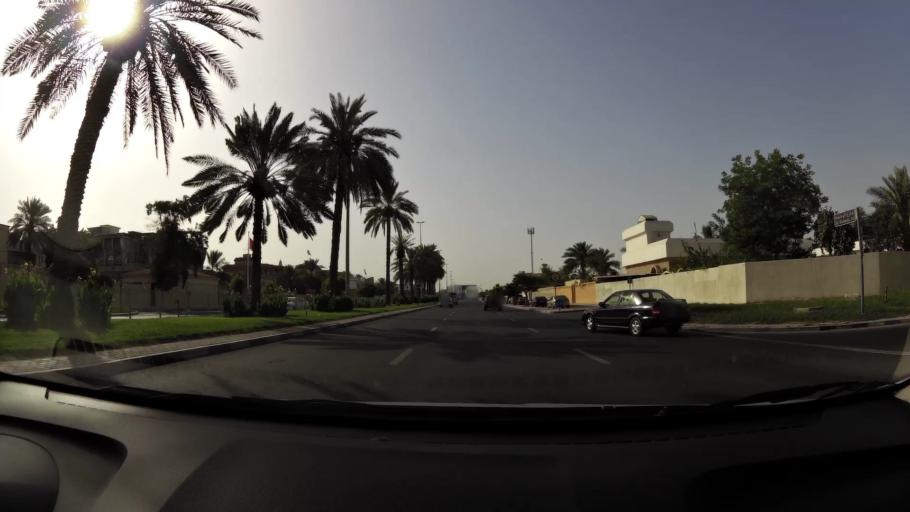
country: AE
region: Ash Shariqah
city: Sharjah
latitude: 25.2933
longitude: 55.3417
